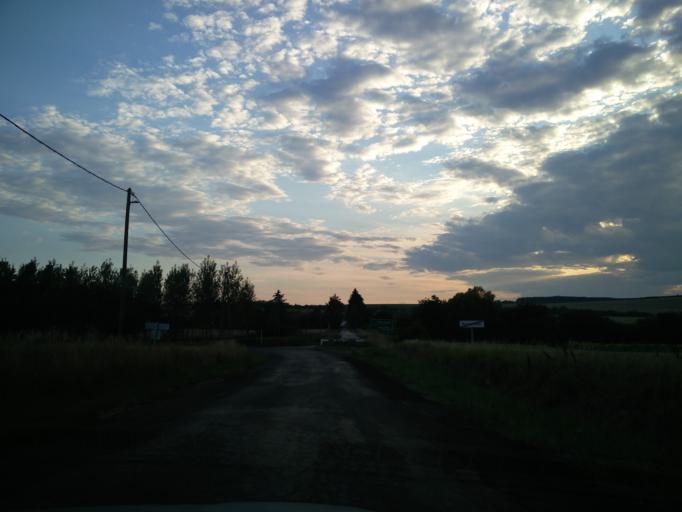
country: HU
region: Zala
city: Zalaszentgrot
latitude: 47.0021
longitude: 16.9667
